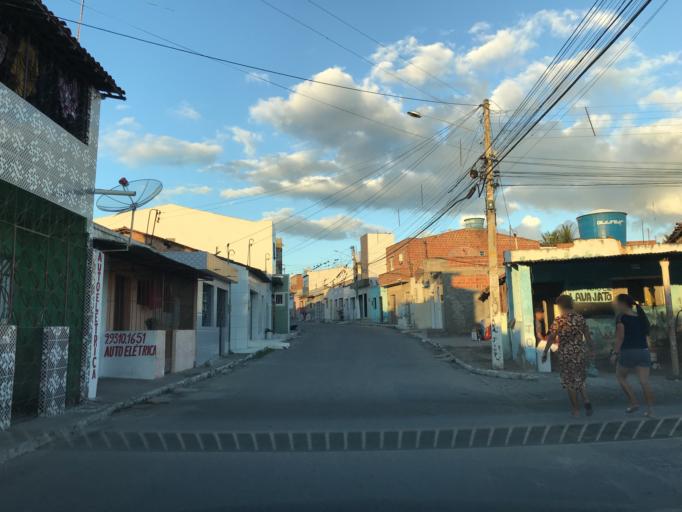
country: BR
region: Pernambuco
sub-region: Bezerros
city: Bezerros
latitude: -8.2378
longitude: -35.7584
